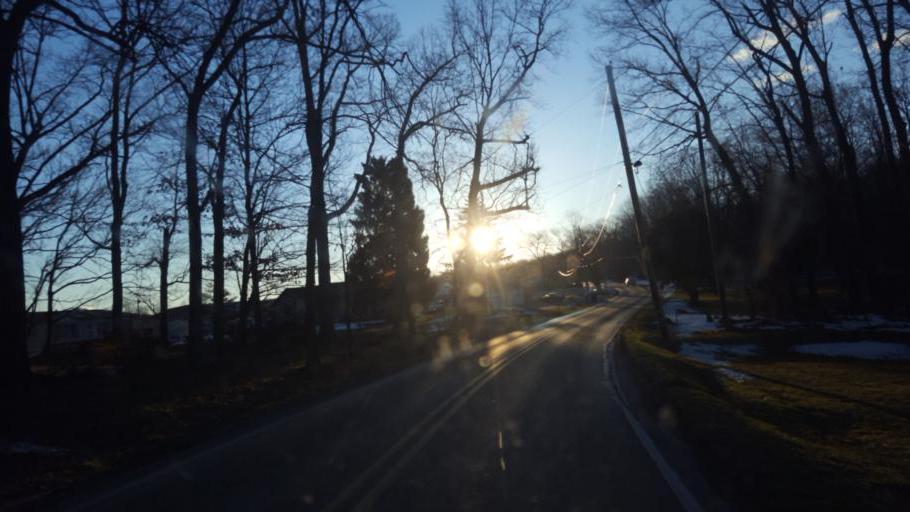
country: US
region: Pennsylvania
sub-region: Lancaster County
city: East Earl
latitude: 40.0759
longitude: -76.0530
